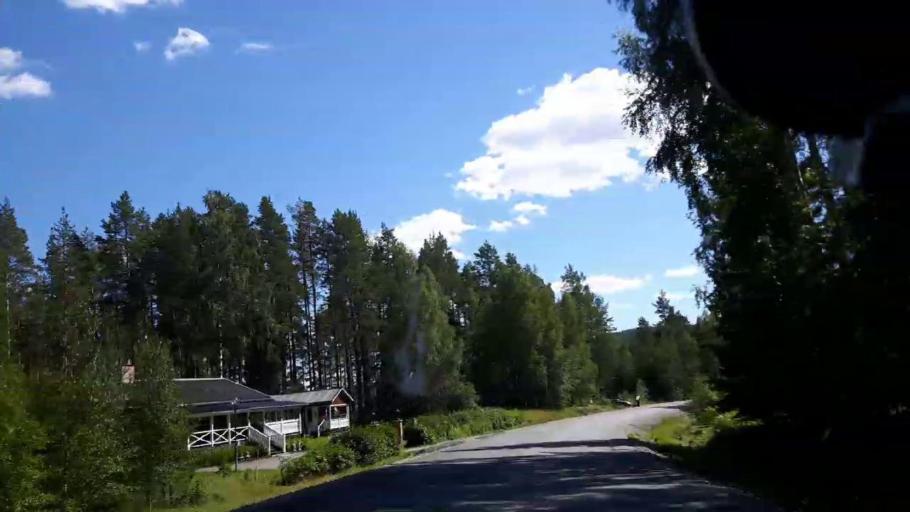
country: SE
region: Vaesternorrland
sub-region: Ange Kommun
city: Fransta
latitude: 62.6987
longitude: 16.3910
